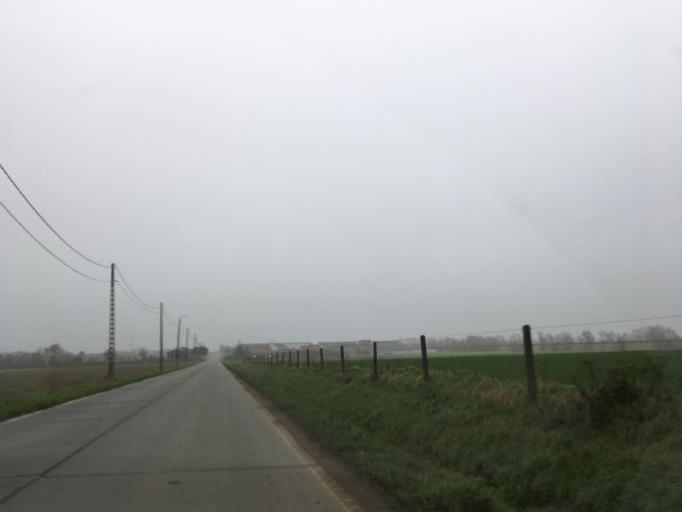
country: BE
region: Flanders
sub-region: Provincie West-Vlaanderen
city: Ardooie
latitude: 50.9941
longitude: 3.1698
